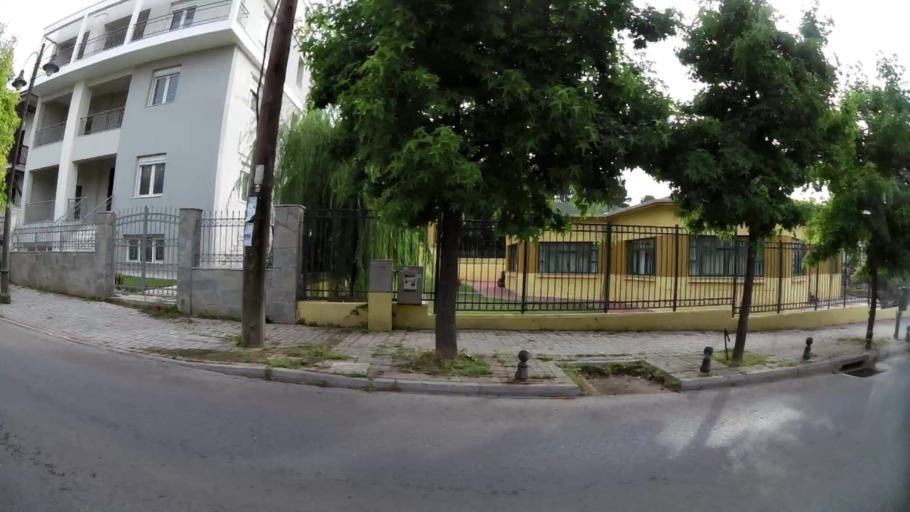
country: GR
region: Central Macedonia
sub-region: Nomos Thessalonikis
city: Thermi
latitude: 40.5476
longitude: 23.0257
